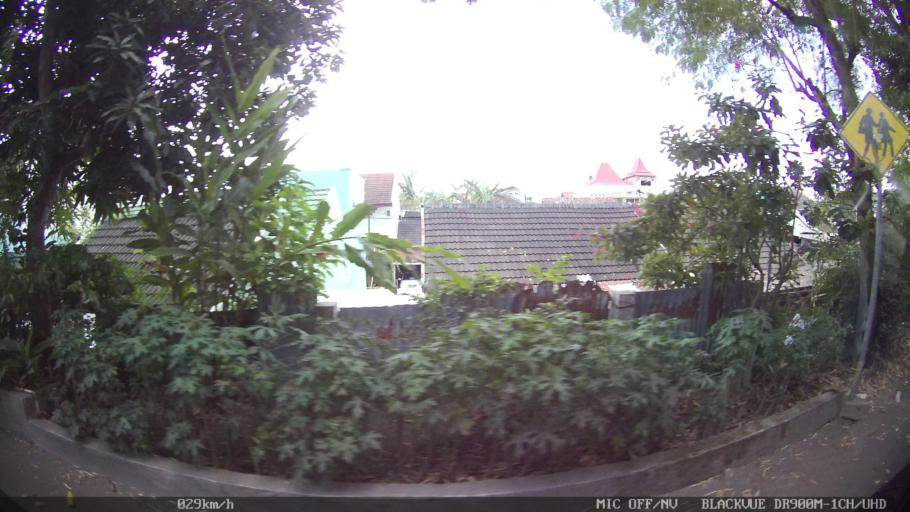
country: ID
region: Daerah Istimewa Yogyakarta
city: Yogyakarta
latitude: -7.8223
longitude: 110.3978
